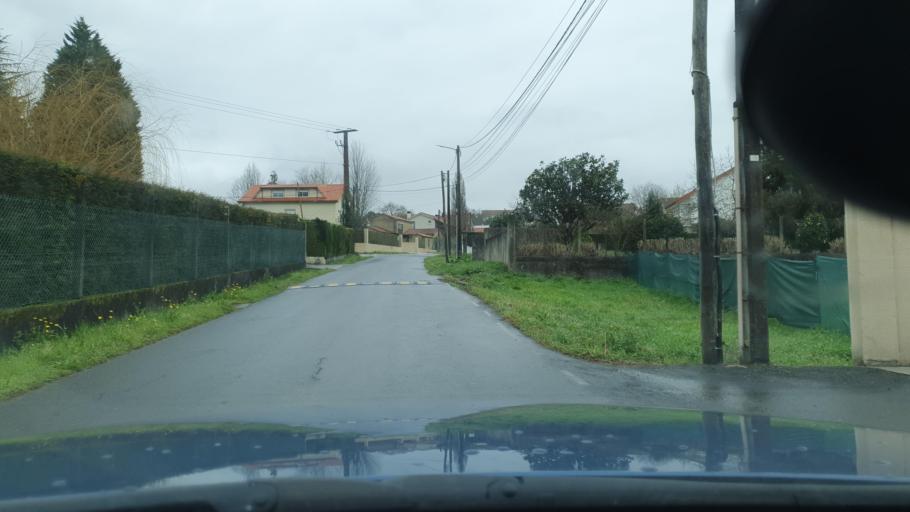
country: ES
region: Galicia
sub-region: Provincia da Coruna
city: Ames
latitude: 42.8321
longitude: -8.6067
